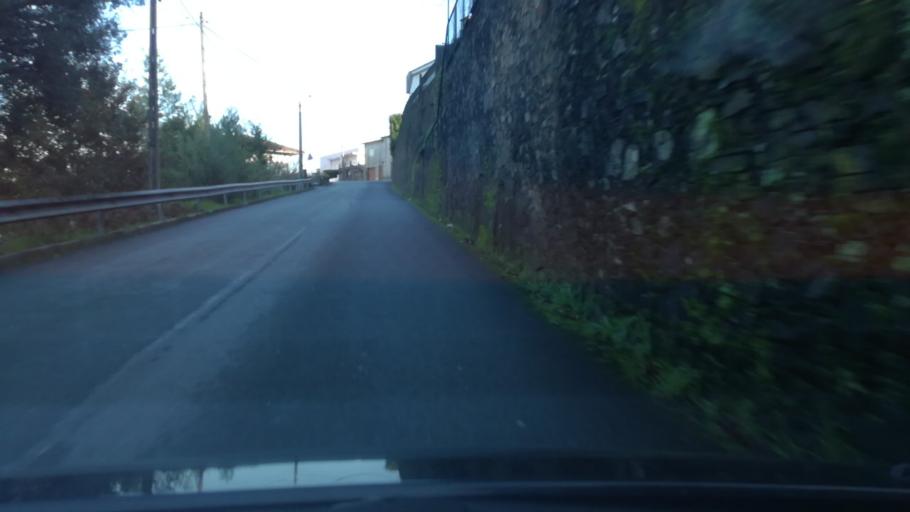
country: PT
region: Braga
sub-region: Vila Nova de Famalicao
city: Ferreiros
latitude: 41.3488
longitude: -8.5287
